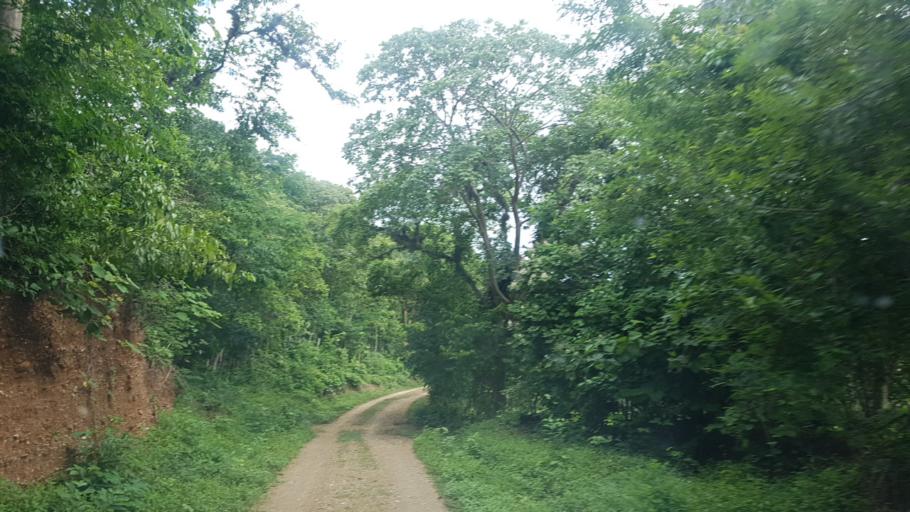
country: NI
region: Nueva Segovia
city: Ciudad Antigua
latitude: 13.6000
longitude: -86.3630
